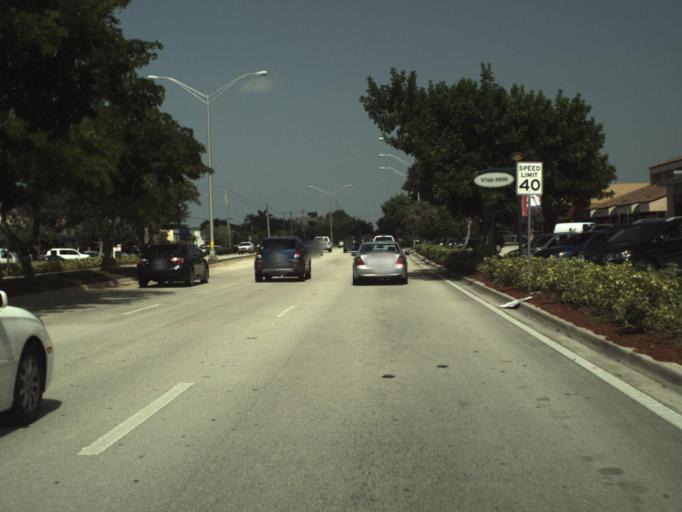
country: US
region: Florida
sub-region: Broward County
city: Coral Springs
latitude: 26.2724
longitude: -80.2576
